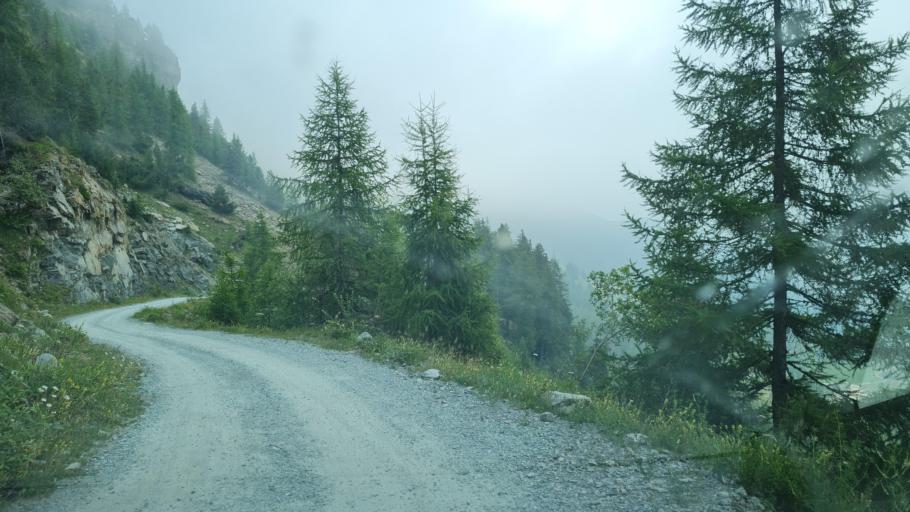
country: IT
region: Aosta Valley
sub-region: Valle d'Aosta
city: Champorcher
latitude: 45.6264
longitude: 7.5953
